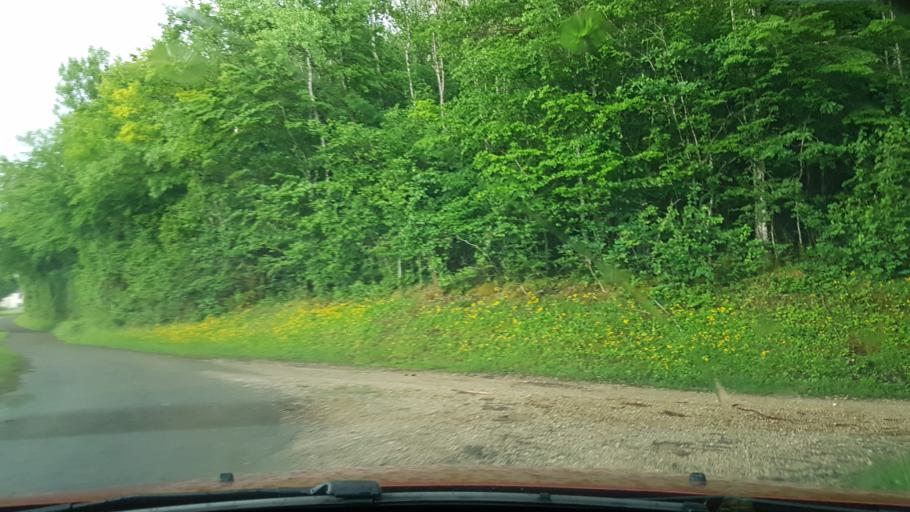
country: FR
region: Franche-Comte
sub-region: Departement du Jura
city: Clairvaux-les-Lacs
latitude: 46.5326
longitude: 5.7073
